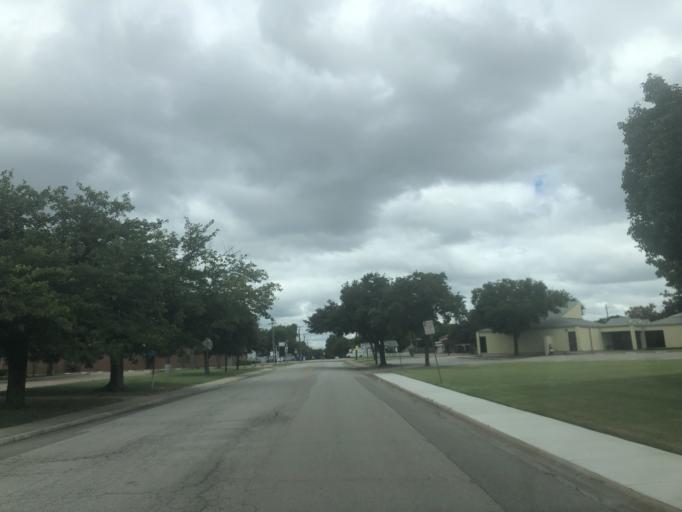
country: US
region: Texas
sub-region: Dallas County
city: Duncanville
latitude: 32.6451
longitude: -96.9068
